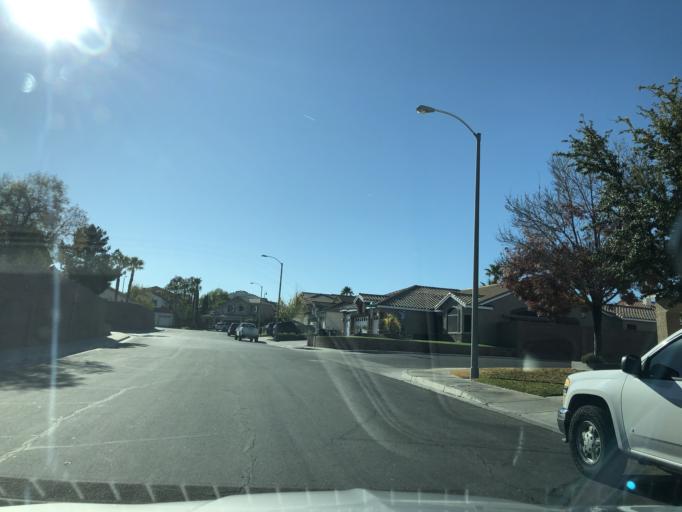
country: US
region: Nevada
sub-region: Clark County
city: Whitney
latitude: 36.0100
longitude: -115.0844
